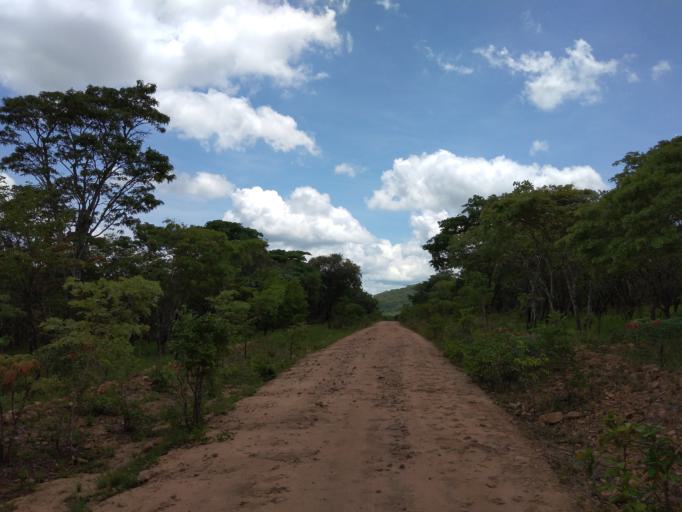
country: ZM
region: Central
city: Mkushi
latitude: -13.9099
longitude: 29.8656
